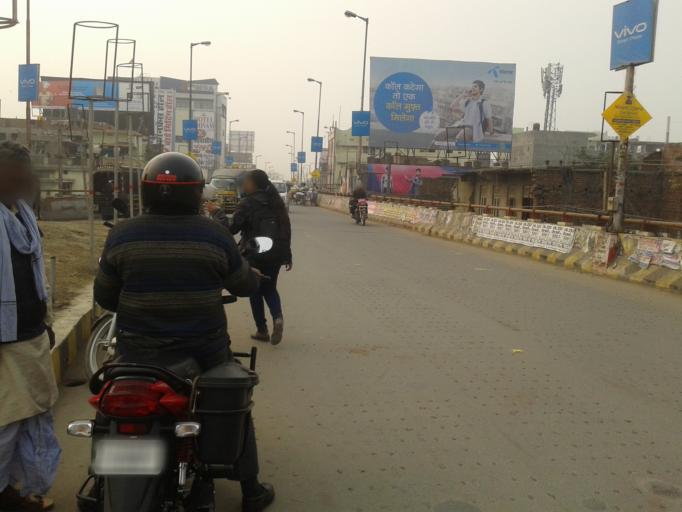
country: IN
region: Bihar
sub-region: Muzaffarpur
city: Muzaffarpur
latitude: 26.1198
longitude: 85.3858
